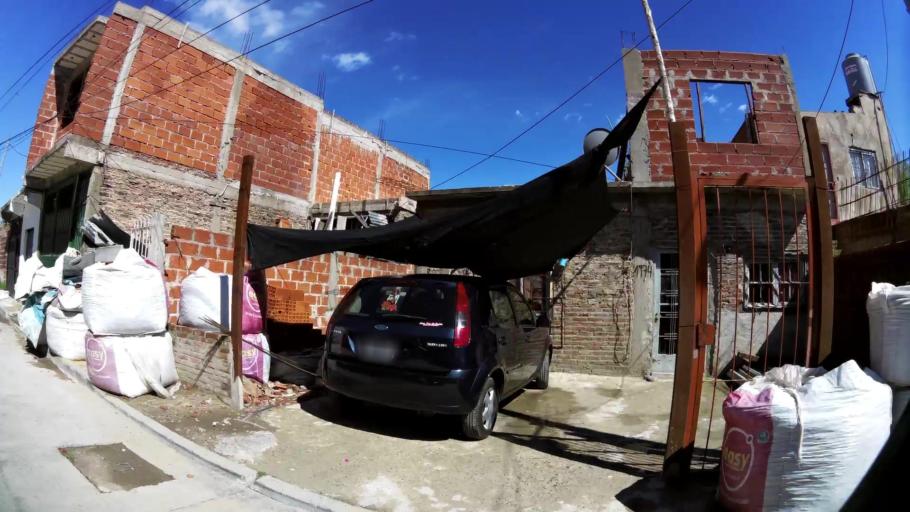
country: AR
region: Buenos Aires
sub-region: Partido de Quilmes
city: Quilmes
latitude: -34.6864
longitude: -58.3022
